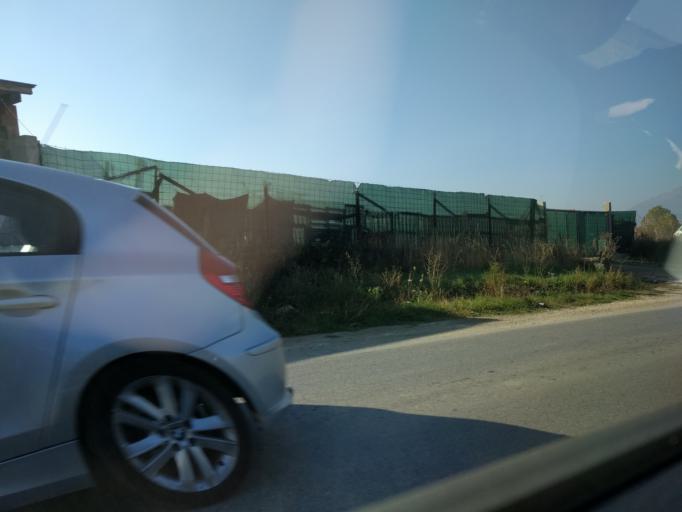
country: XK
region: Prizren
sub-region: Prizren
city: Prizren
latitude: 42.2493
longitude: 20.7276
